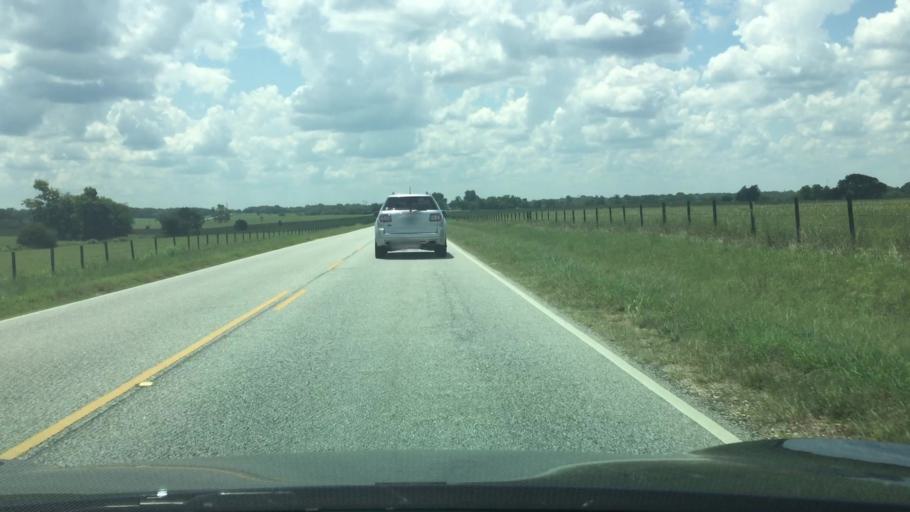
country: US
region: Alabama
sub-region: Montgomery County
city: Pike Road
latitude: 32.2709
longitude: -86.0998
